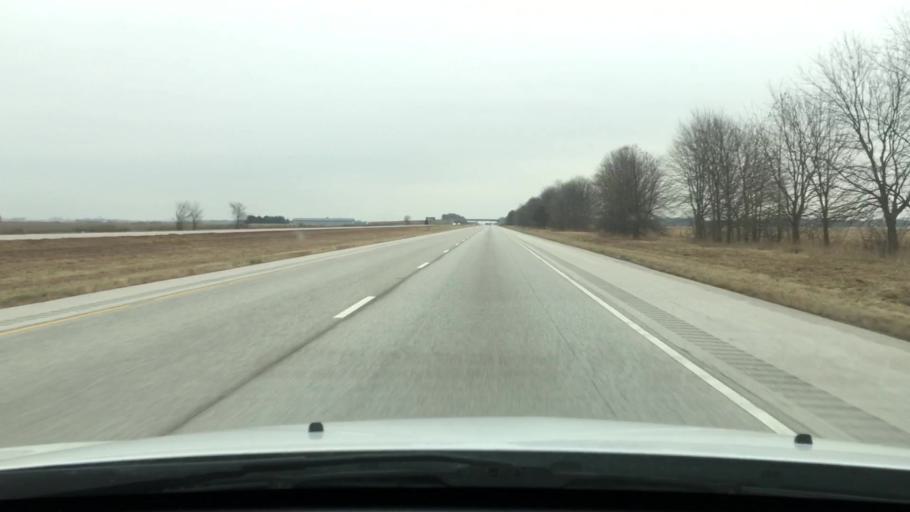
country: US
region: Illinois
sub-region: Morgan County
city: South Jacksonville
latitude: 39.6805
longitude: -90.3410
